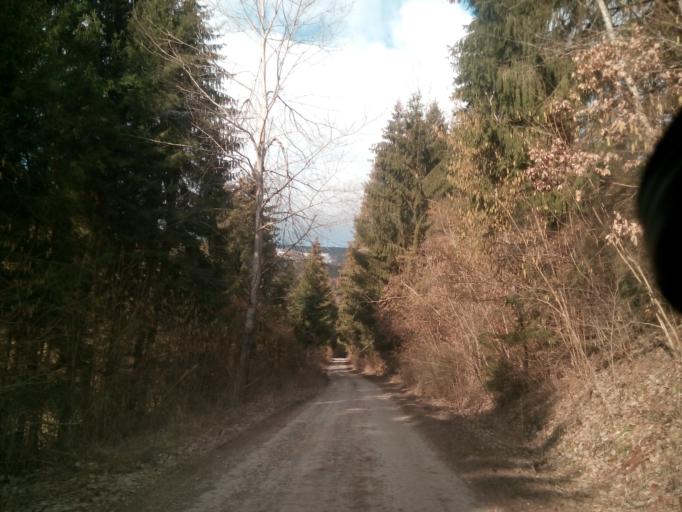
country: SK
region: Banskobystricky
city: Revuca
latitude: 48.7308
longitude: 20.2300
